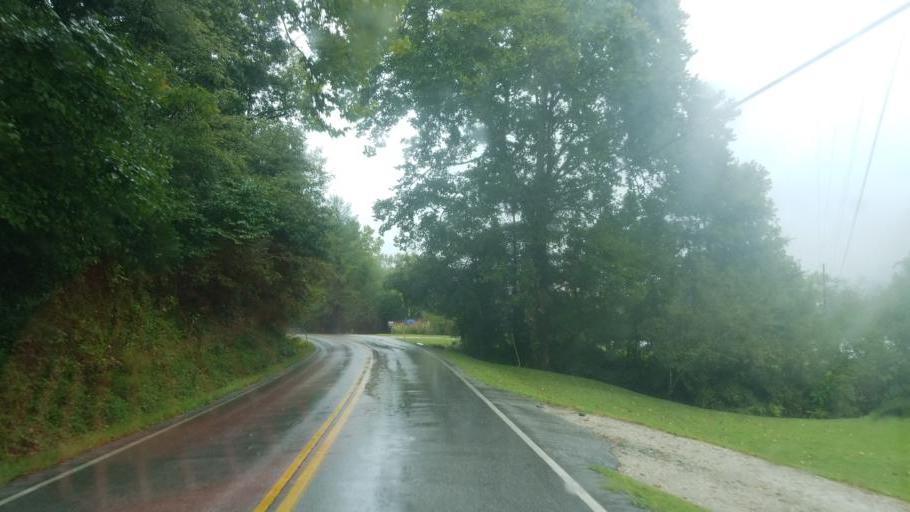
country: US
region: Ohio
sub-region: Scioto County
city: Franklin Furnace
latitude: 38.6609
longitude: -82.9182
